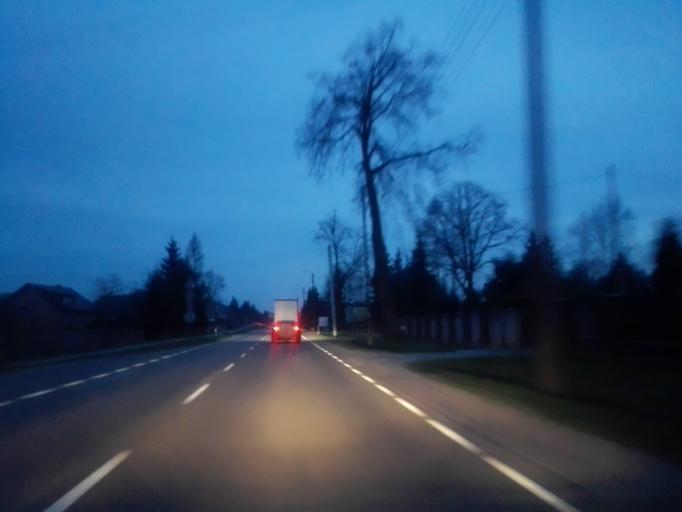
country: PL
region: Podlasie
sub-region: Lomza
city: Lomza
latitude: 53.1329
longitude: 22.0410
